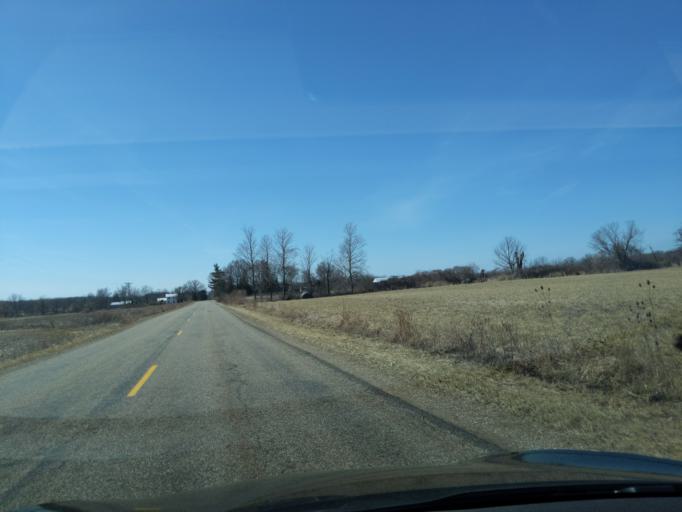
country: US
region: Michigan
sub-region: Ionia County
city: Lake Odessa
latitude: 42.7125
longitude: -85.0678
